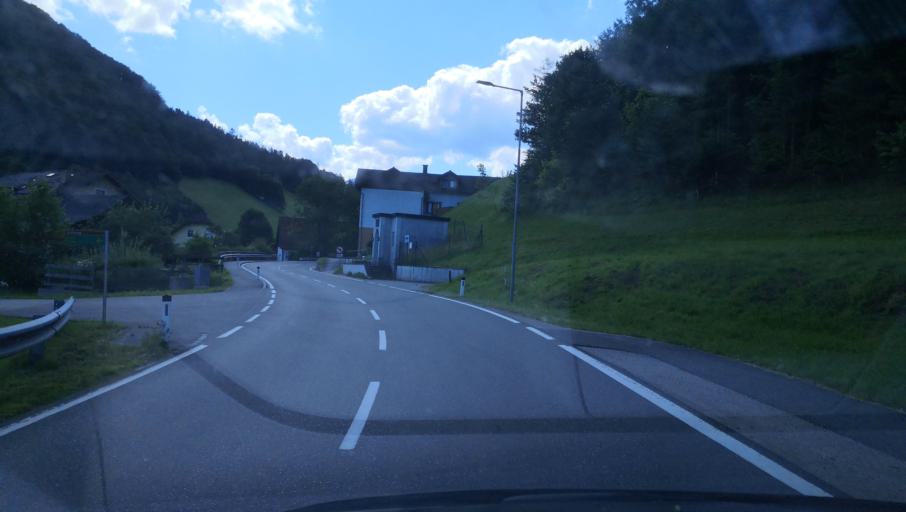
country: AT
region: Lower Austria
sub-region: Politischer Bezirk Scheibbs
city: Gresten
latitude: 47.9685
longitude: 15.0210
